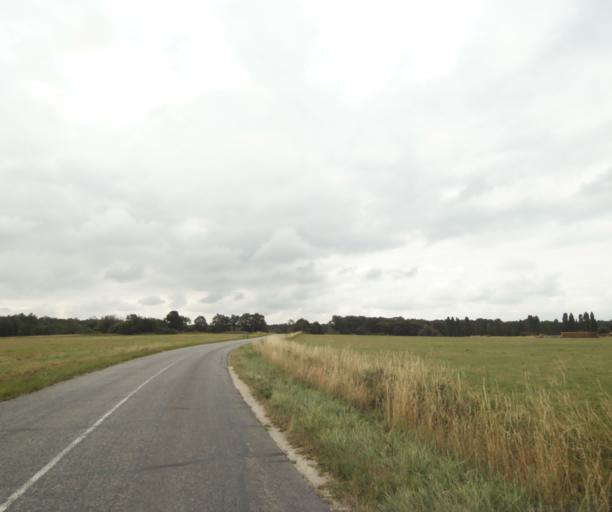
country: FR
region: Centre
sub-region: Departement du Loiret
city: Chanteau
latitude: 47.9663
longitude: 1.9764
